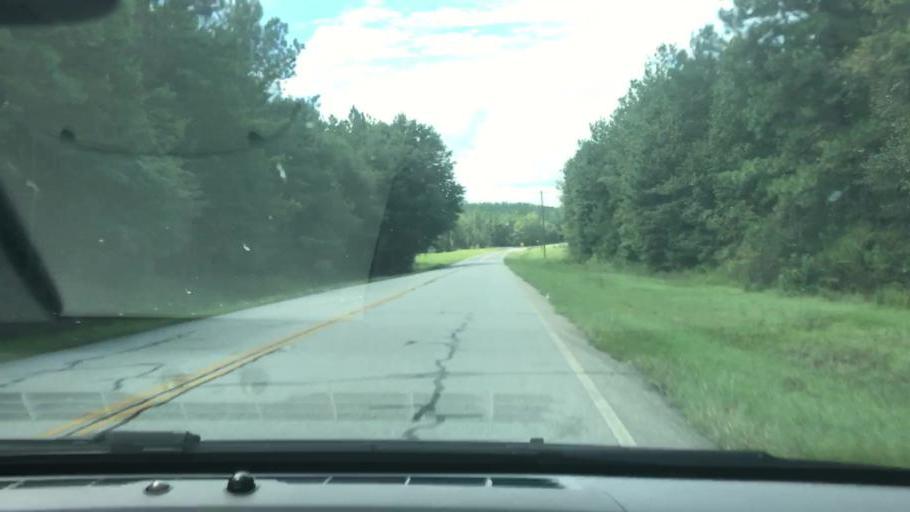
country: US
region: Georgia
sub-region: Stewart County
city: Lumpkin
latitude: 32.1417
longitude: -84.9321
